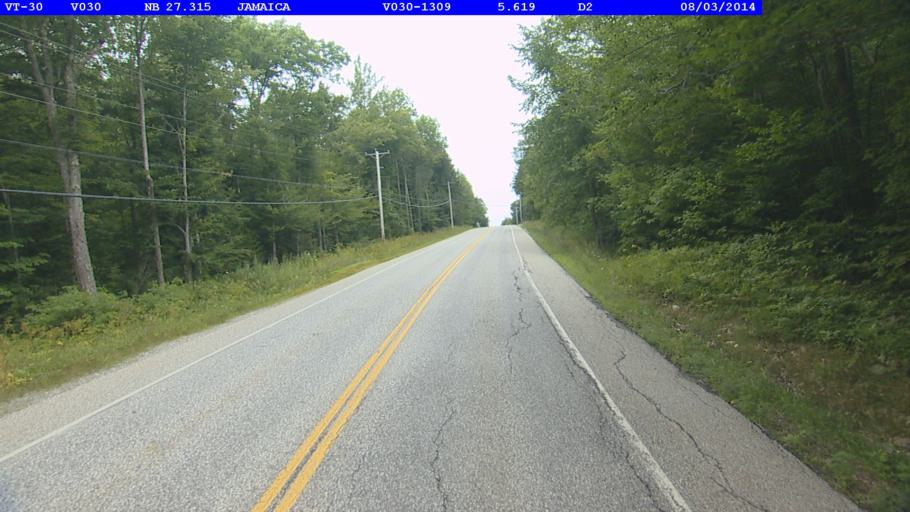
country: US
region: Vermont
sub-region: Windham County
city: Dover
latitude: 43.1137
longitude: -72.8021
